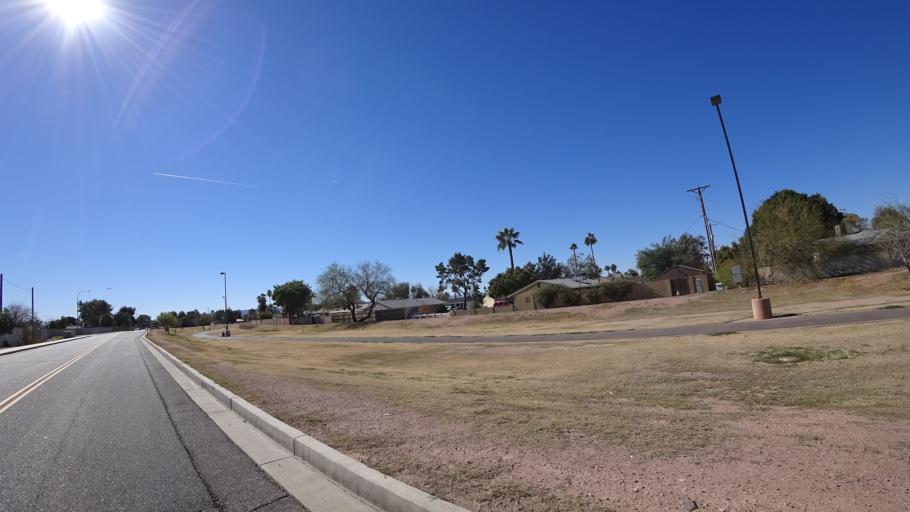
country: US
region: Arizona
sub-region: Maricopa County
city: Tempe Junction
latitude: 33.4691
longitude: -111.9782
